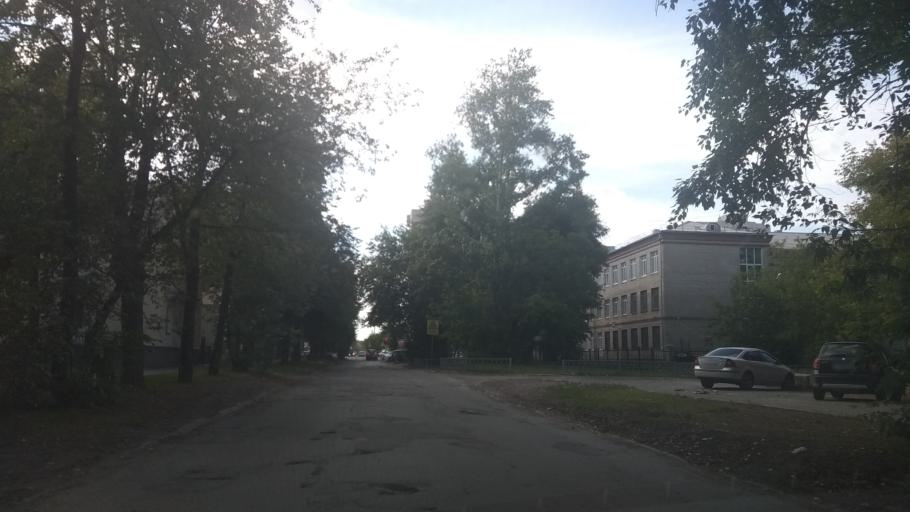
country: RU
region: Sverdlovsk
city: Yekaterinburg
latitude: 56.9010
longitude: 60.5857
